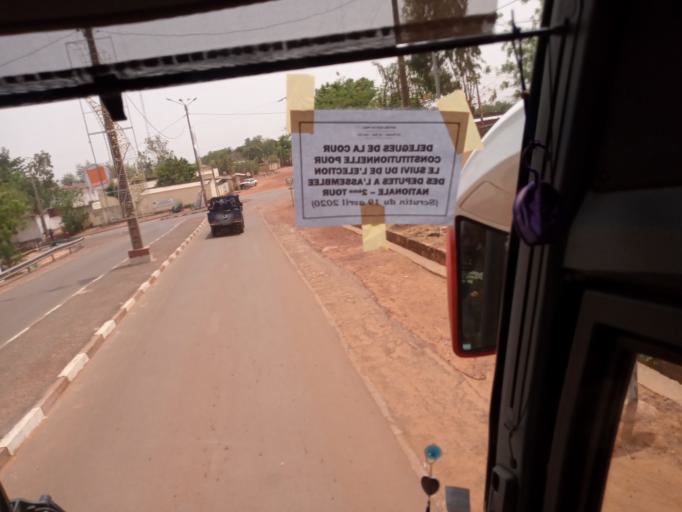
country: ML
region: Koulikoro
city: Koulikoro
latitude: 12.8607
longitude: -7.5603
